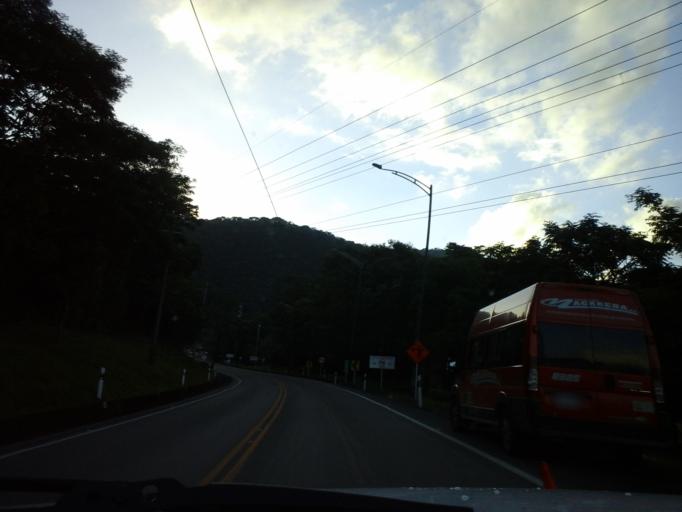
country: CO
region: Meta
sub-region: Villavicencio
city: Villavicencio
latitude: 4.1406
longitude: -73.6577
